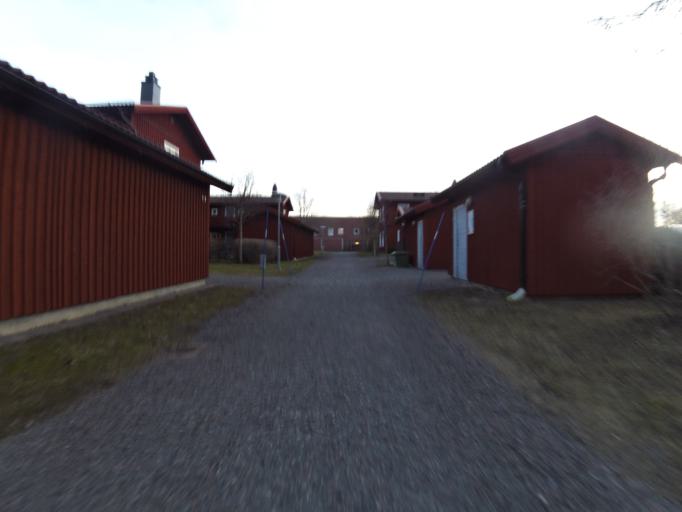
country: SE
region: Gaevleborg
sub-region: Gavle Kommun
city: Gavle
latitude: 60.6612
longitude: 17.1653
